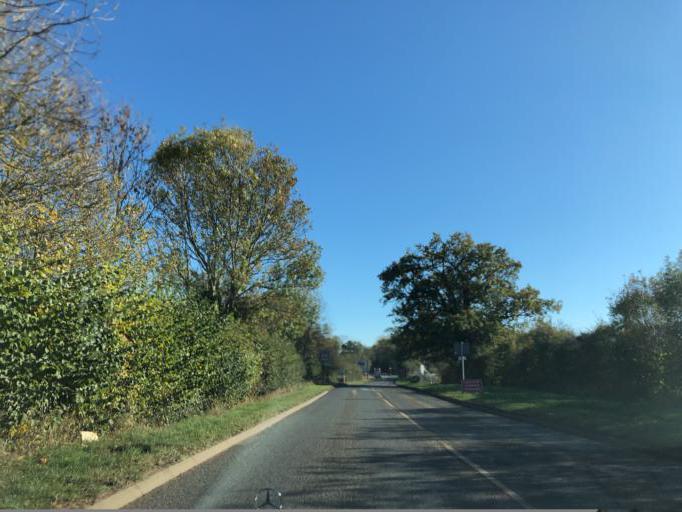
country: GB
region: England
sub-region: Warwickshire
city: Royal Leamington Spa
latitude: 52.2622
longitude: -1.5393
